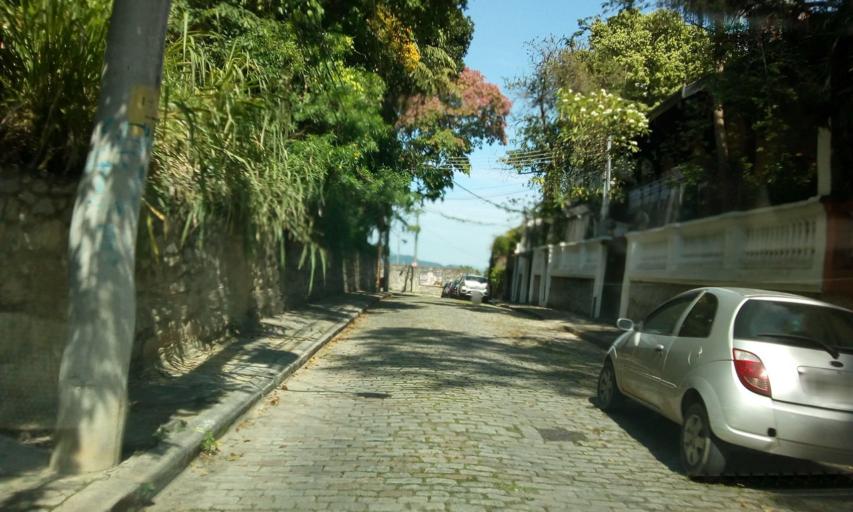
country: BR
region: Rio de Janeiro
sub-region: Rio De Janeiro
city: Rio de Janeiro
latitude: -22.9175
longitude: -43.1834
